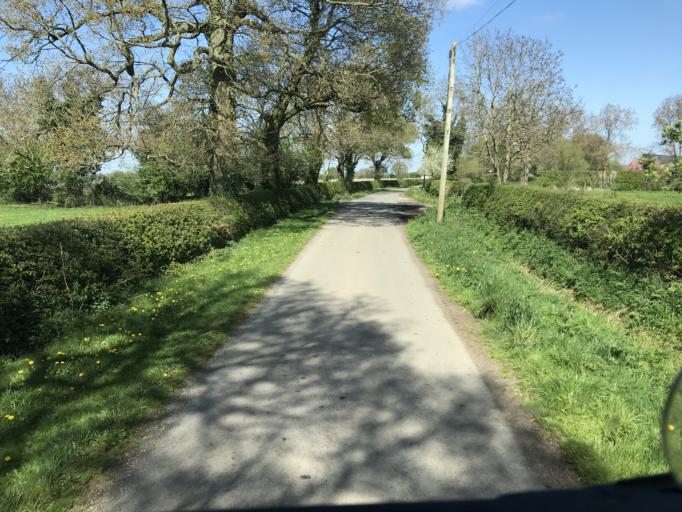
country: GB
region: England
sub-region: Cheshire East
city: Nantwich
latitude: 53.1072
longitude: -2.5313
